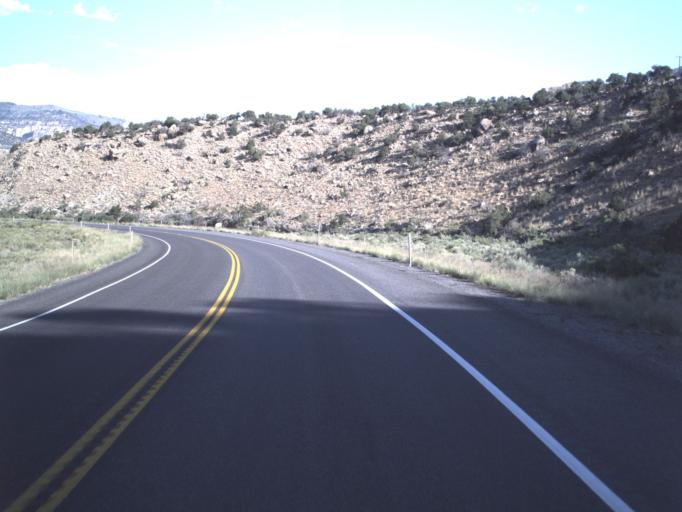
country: US
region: Utah
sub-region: Emery County
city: Huntington
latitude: 39.3674
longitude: -111.0506
